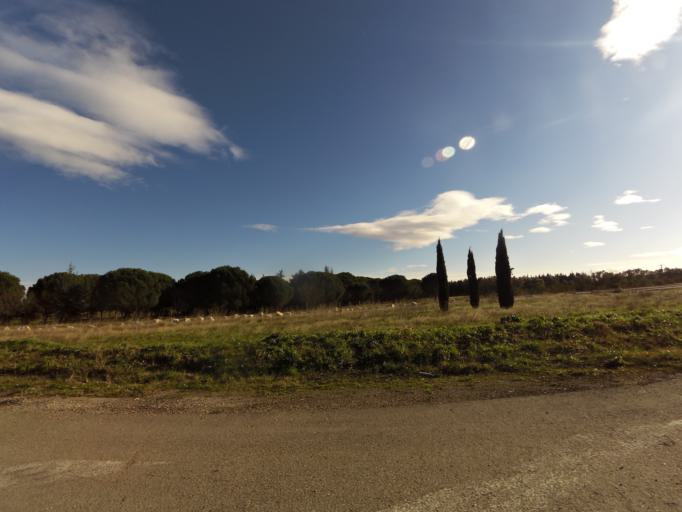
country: FR
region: Languedoc-Roussillon
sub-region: Departement du Gard
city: Codognan
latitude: 43.7354
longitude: 4.2362
